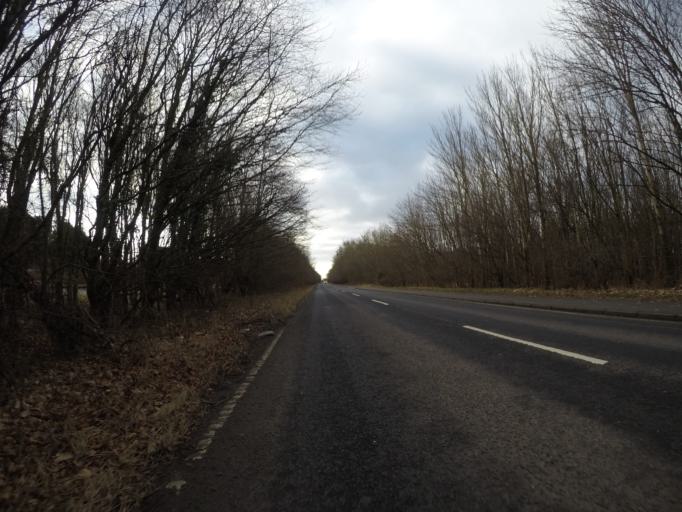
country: GB
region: Scotland
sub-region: North Ayrshire
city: Dreghorn
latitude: 55.5813
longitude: -4.6445
